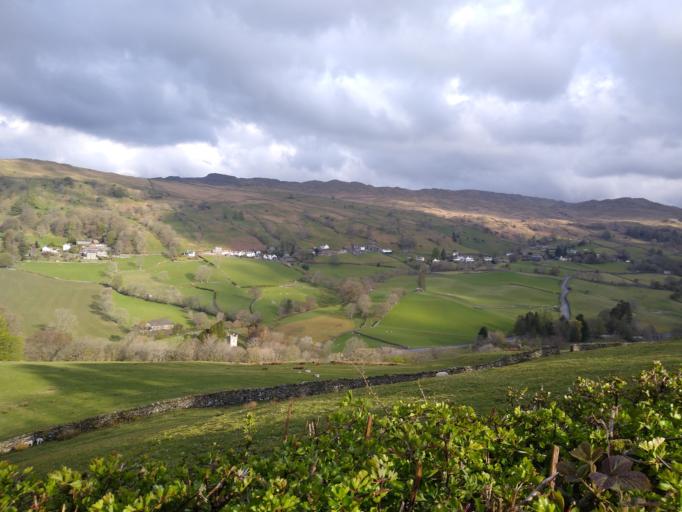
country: GB
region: England
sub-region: Cumbria
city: Windermere
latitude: 54.4153
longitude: -2.9019
